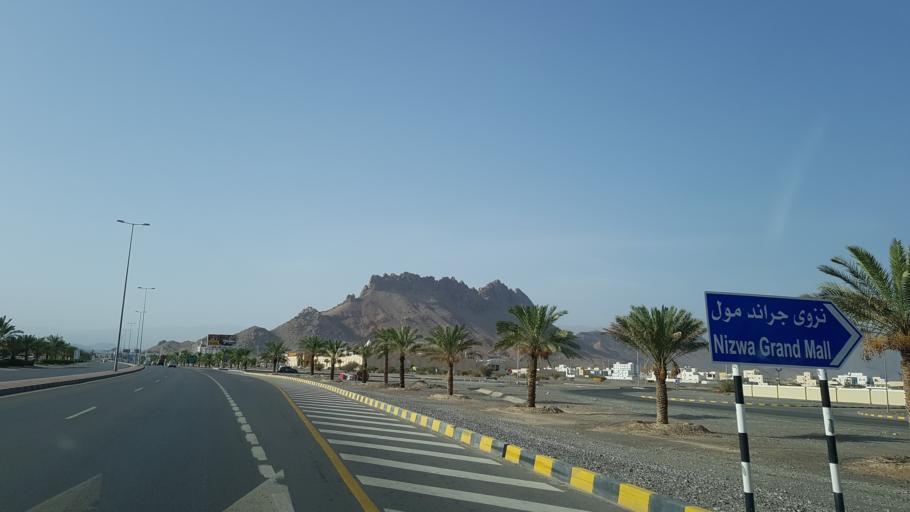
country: OM
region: Muhafazat ad Dakhiliyah
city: Nizwa
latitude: 22.8656
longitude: 57.5378
